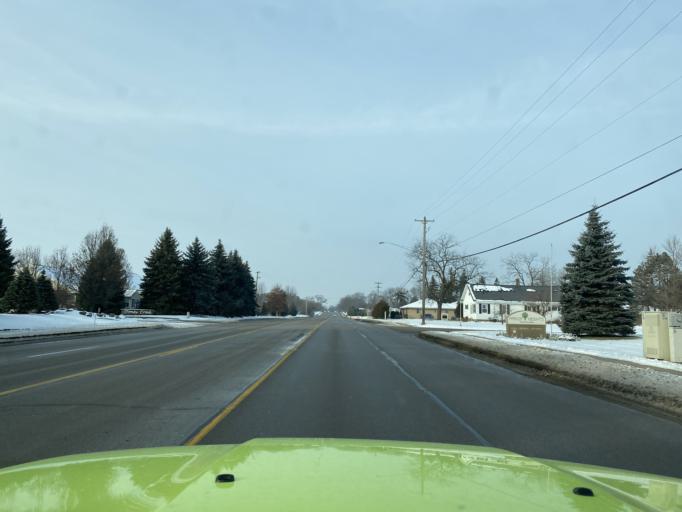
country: US
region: Michigan
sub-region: Ottawa County
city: Hudsonville
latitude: 42.8877
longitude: -85.8552
